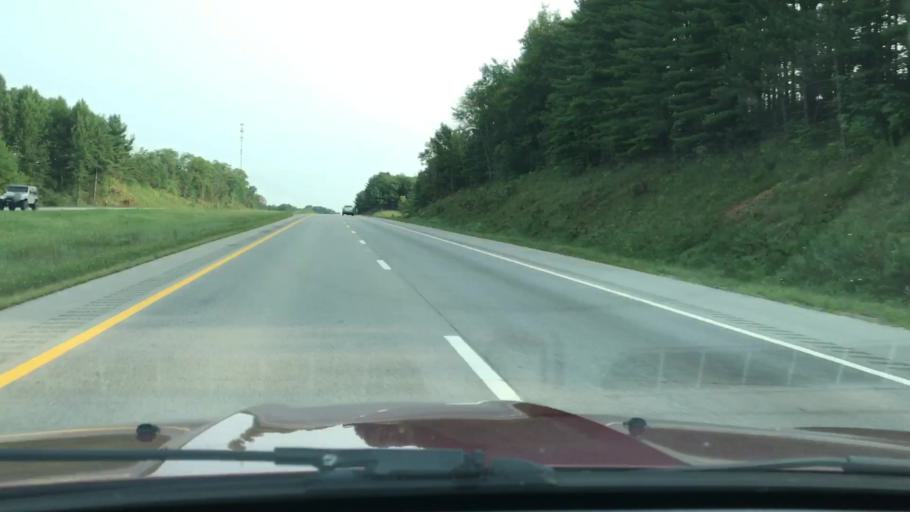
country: US
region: Ohio
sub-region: Noble County
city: Caldwell
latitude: 39.8448
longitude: -81.5441
